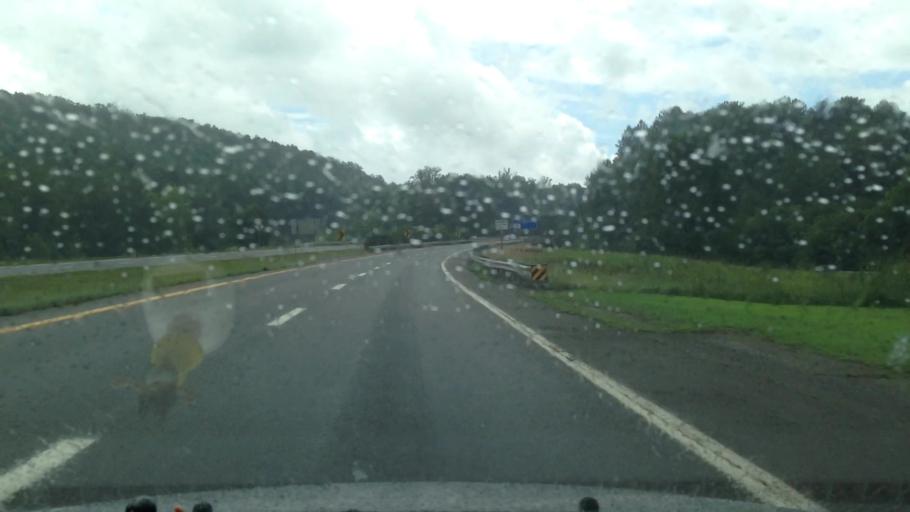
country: US
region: Virginia
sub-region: Henry County
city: Collinsville
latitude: 36.7285
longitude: -79.9385
